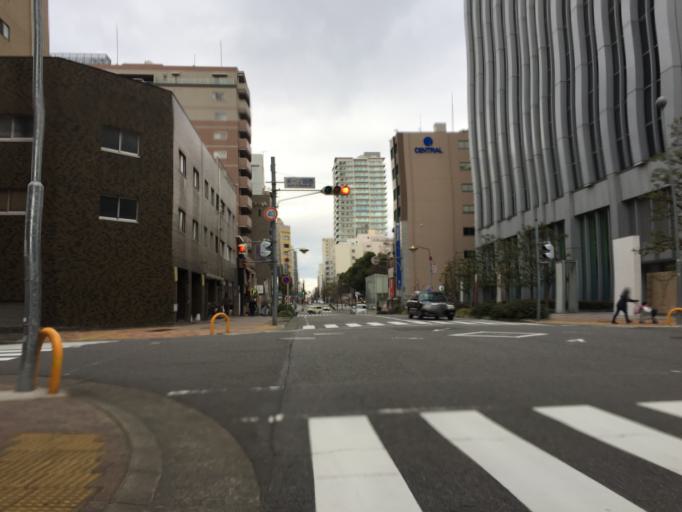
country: JP
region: Aichi
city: Nagoya-shi
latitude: 35.1758
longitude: 136.9102
